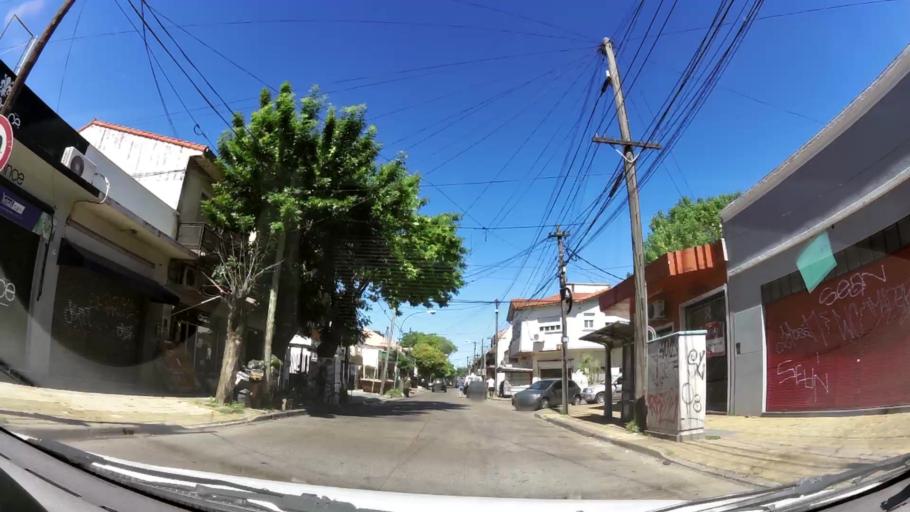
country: AR
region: Buenos Aires
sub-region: Partido de Vicente Lopez
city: Olivos
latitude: -34.5242
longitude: -58.5048
